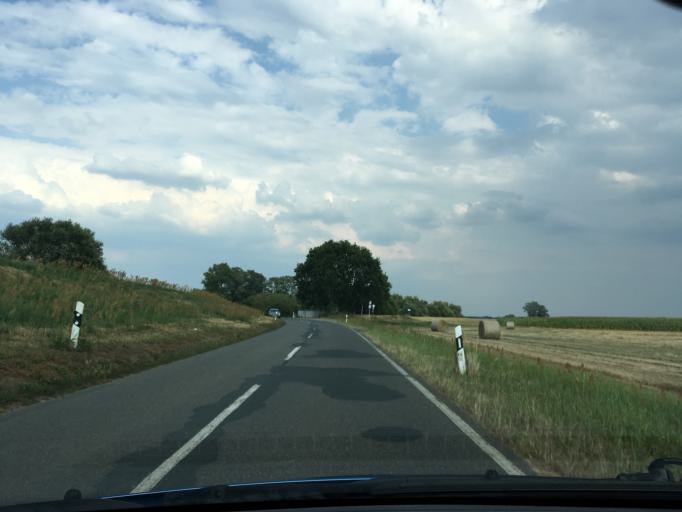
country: DE
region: Lower Saxony
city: Dannenberg
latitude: 53.1342
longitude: 11.0922
